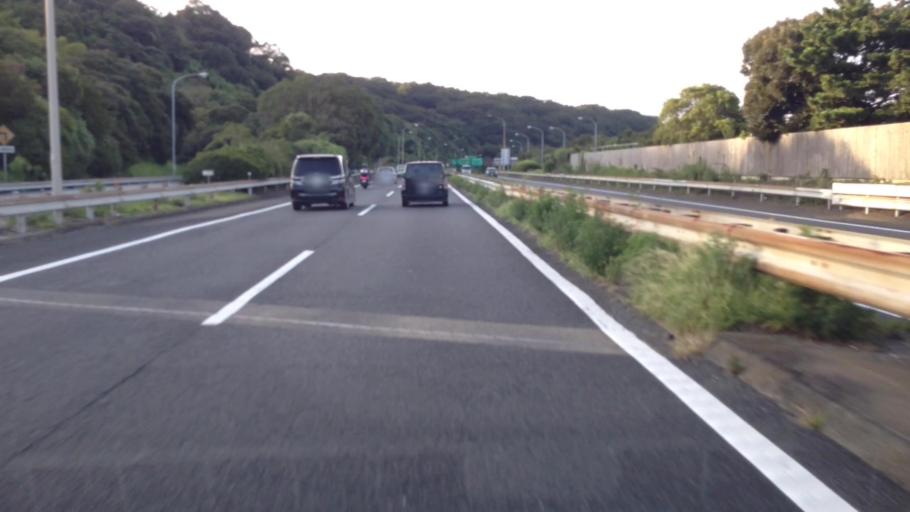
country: JP
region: Kanagawa
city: Zushi
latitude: 35.3350
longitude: 139.5917
